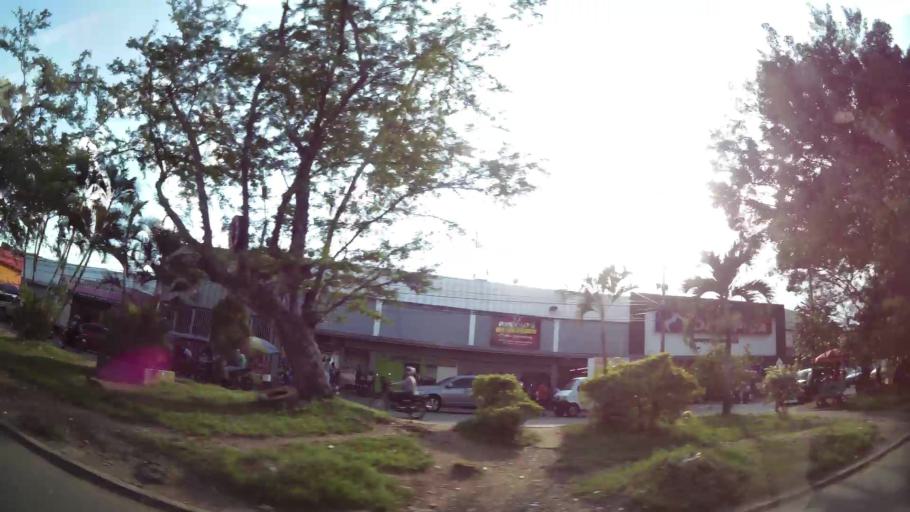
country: CO
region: Valle del Cauca
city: Cali
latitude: 3.4015
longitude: -76.5105
